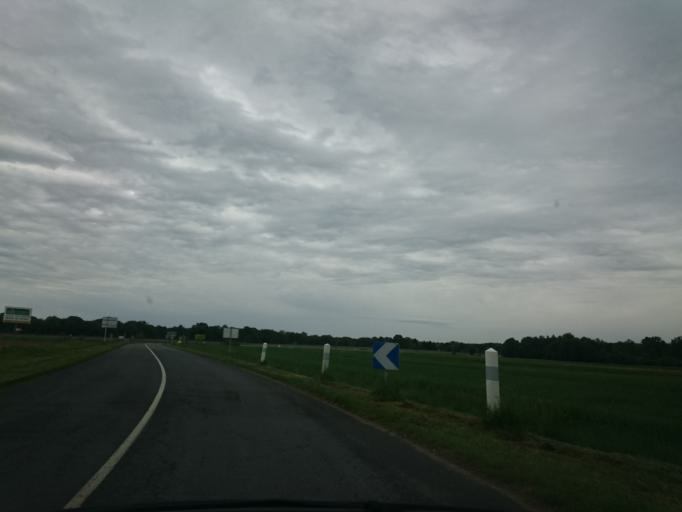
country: FR
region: Centre
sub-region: Departement du Loir-et-Cher
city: Muides-sur-Loire
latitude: 47.6624
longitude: 1.5340
